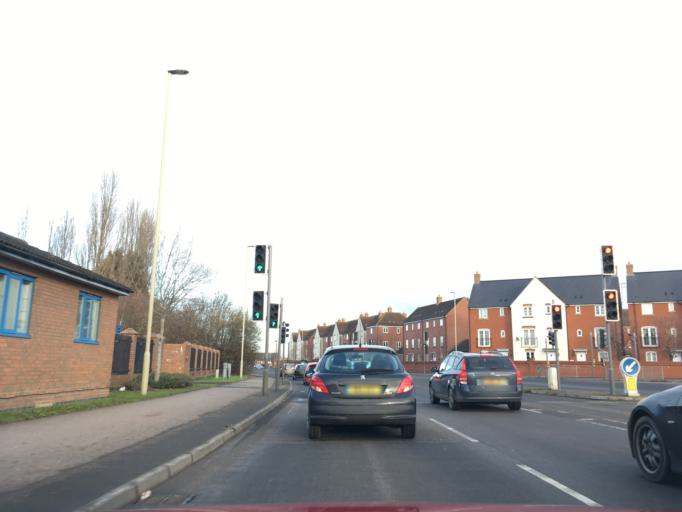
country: GB
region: England
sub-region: Gloucestershire
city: Gloucester
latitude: 51.8543
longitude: -2.2613
